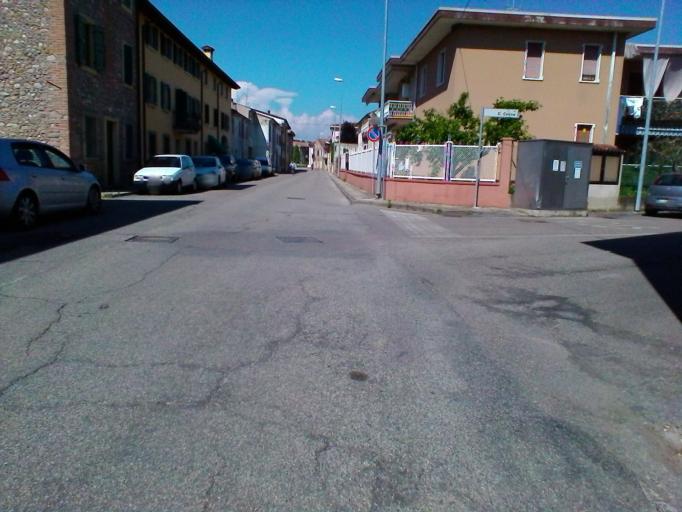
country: IT
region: Veneto
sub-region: Provincia di Verona
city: Povegliano Veronese
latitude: 45.3429
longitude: 10.8813
